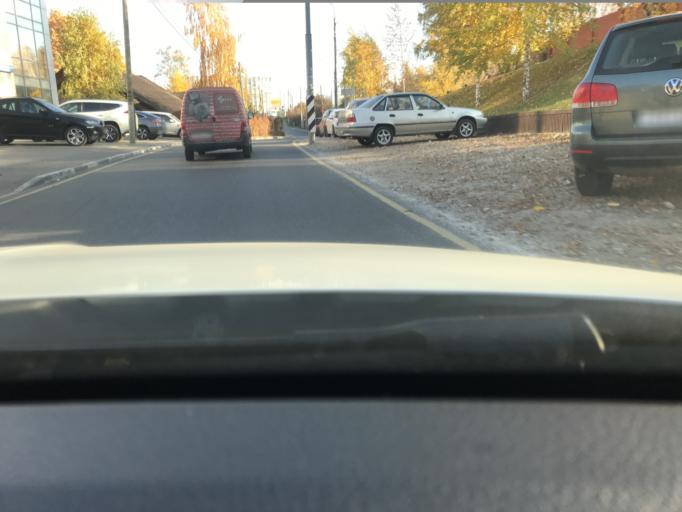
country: RU
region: Moskovskaya
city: Pavshino
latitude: 55.8102
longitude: 37.3778
